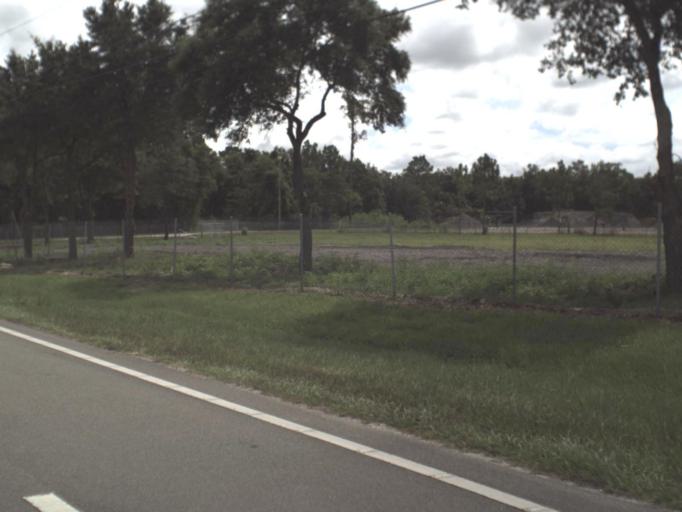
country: US
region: Florida
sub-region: Hernando County
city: Masaryktown
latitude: 28.4148
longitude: -82.4723
